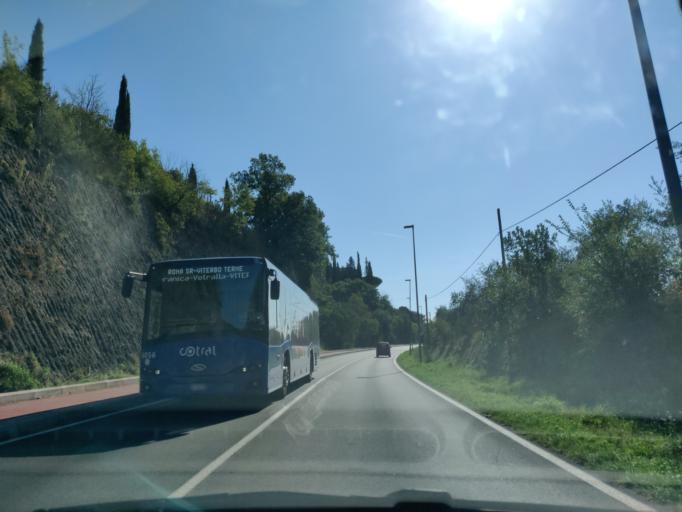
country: IT
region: Latium
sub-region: Provincia di Viterbo
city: Viterbo
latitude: 42.4188
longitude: 12.0853
